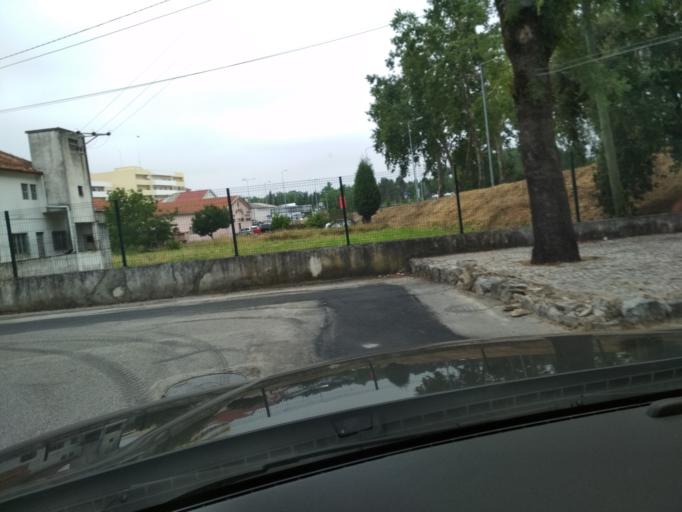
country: PT
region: Aveiro
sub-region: Mealhada
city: Mealhada
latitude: 40.3795
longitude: -8.4496
